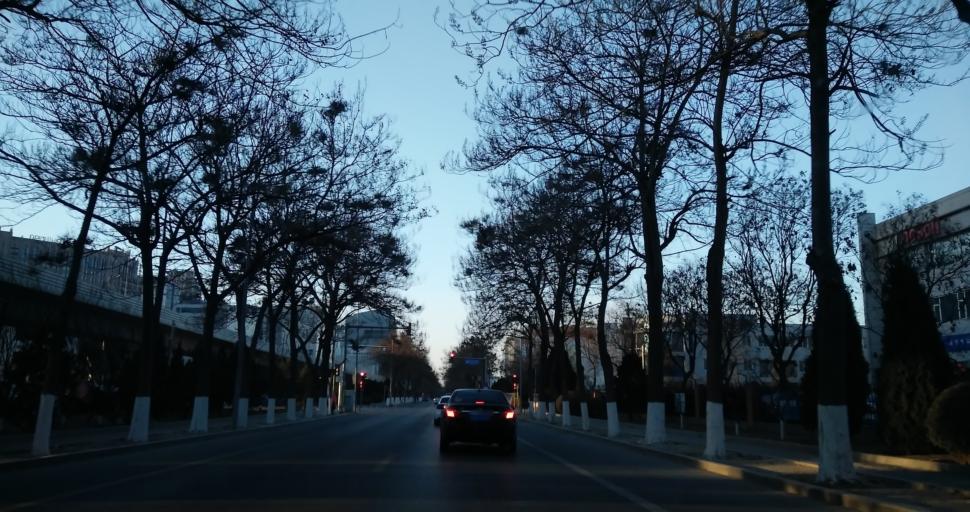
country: CN
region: Beijing
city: Jiugong
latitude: 39.7833
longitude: 116.5149
